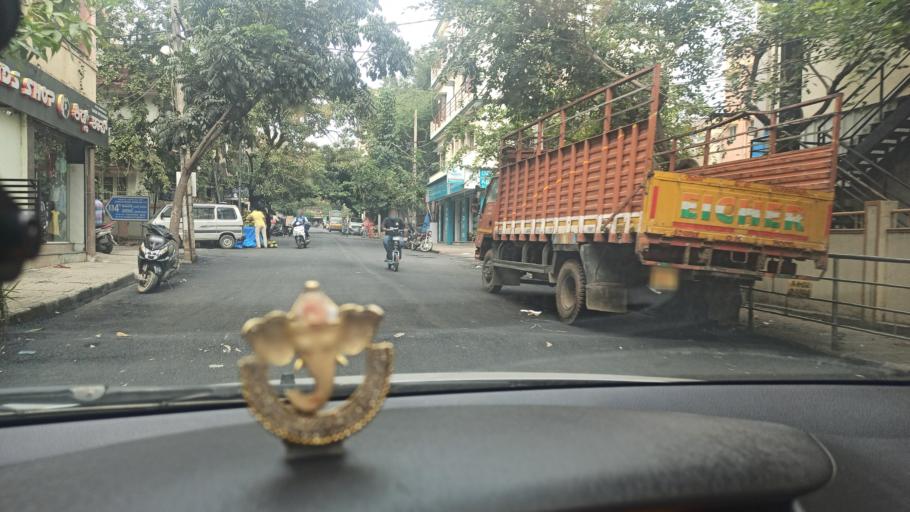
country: IN
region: Karnataka
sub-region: Bangalore Urban
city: Bangalore
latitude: 12.9172
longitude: 77.6318
